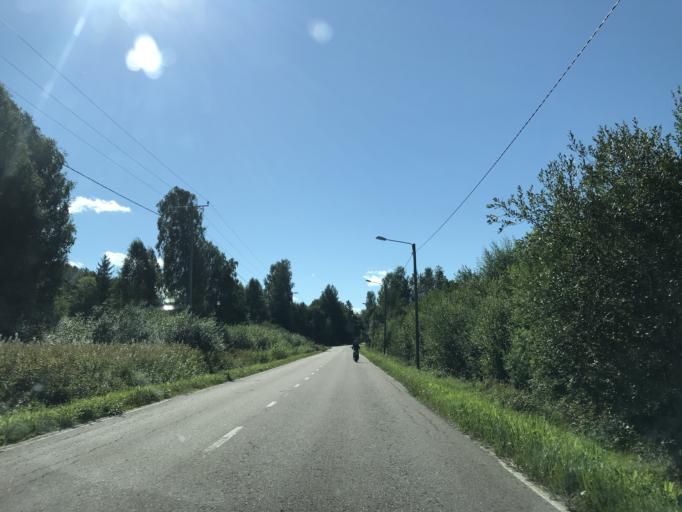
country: FI
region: Uusimaa
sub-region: Helsinki
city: Nurmijaervi
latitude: 60.4877
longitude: 24.6050
